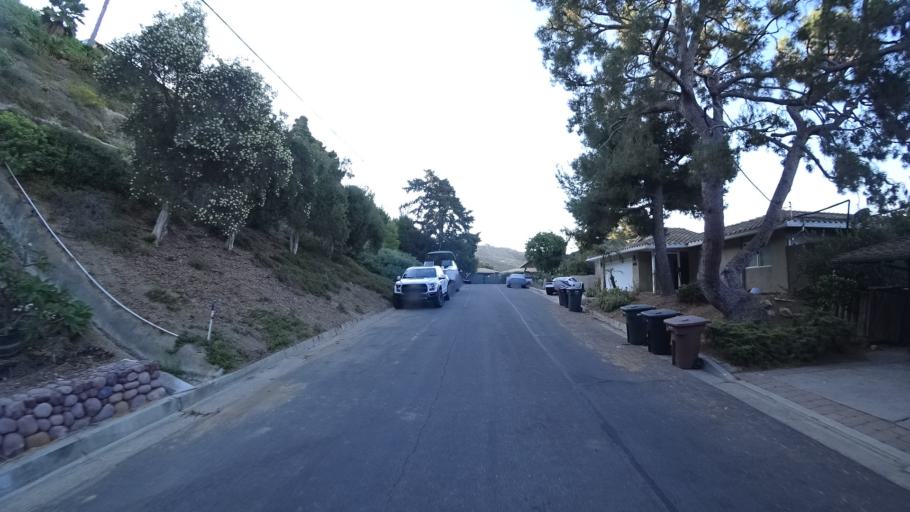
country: US
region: California
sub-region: Orange County
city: San Clemente
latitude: 33.4323
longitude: -117.6036
